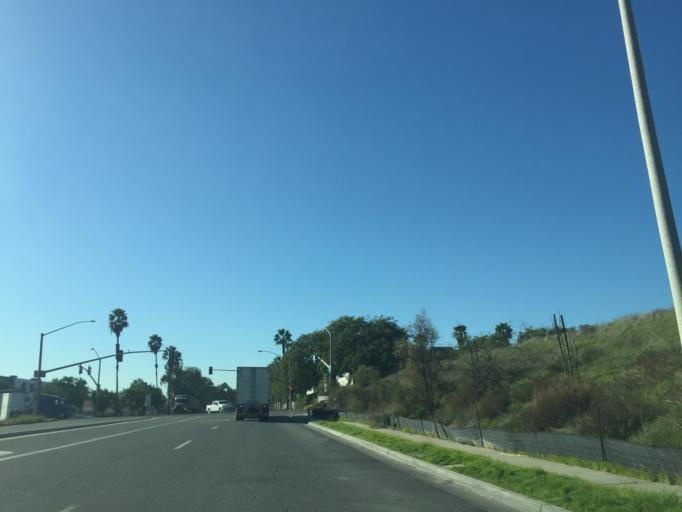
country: MX
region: Baja California
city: Tijuana
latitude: 32.5569
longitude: -116.9269
